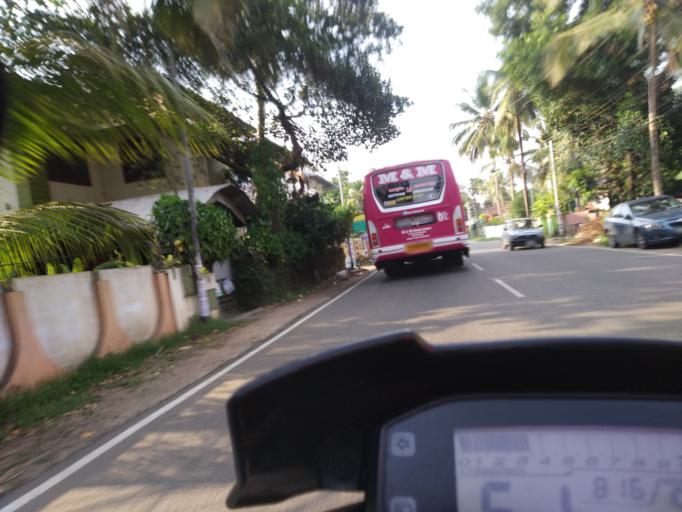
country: IN
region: Kerala
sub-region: Alappuzha
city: Arukutti
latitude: 9.9396
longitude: 76.3511
